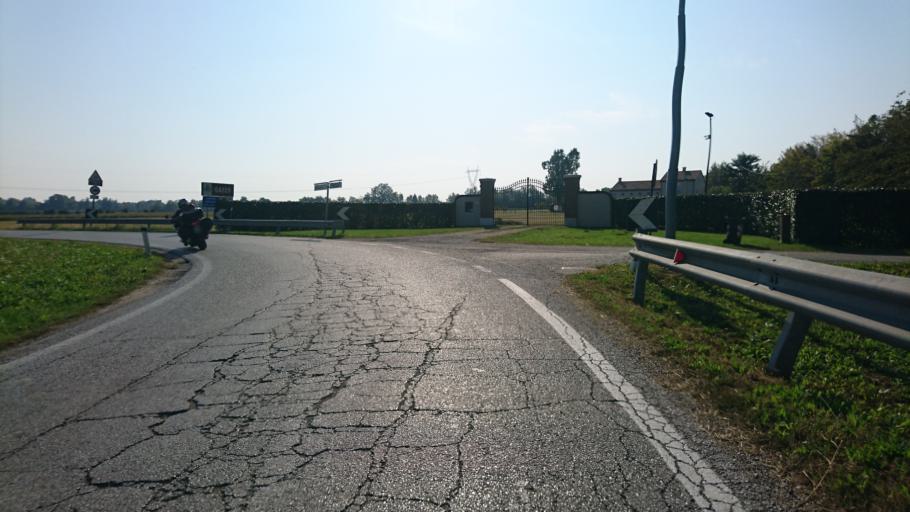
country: IT
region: Veneto
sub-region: Provincia di Padova
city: Gazzo
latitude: 45.5955
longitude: 11.6935
